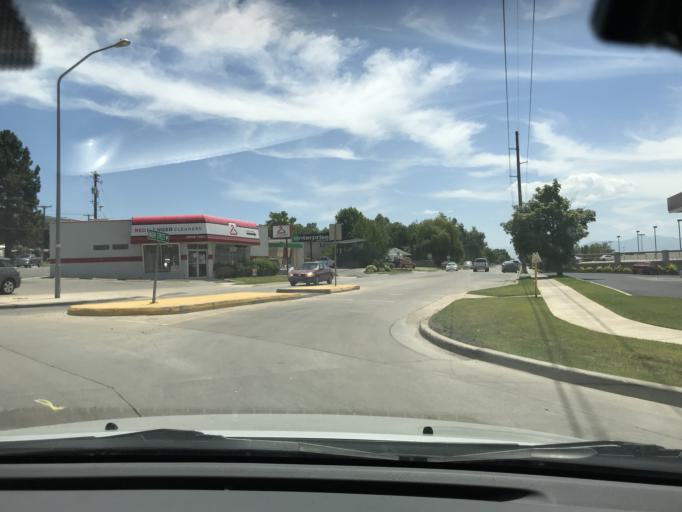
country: US
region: Utah
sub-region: Davis County
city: Woods Cross
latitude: 40.8747
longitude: -111.8859
